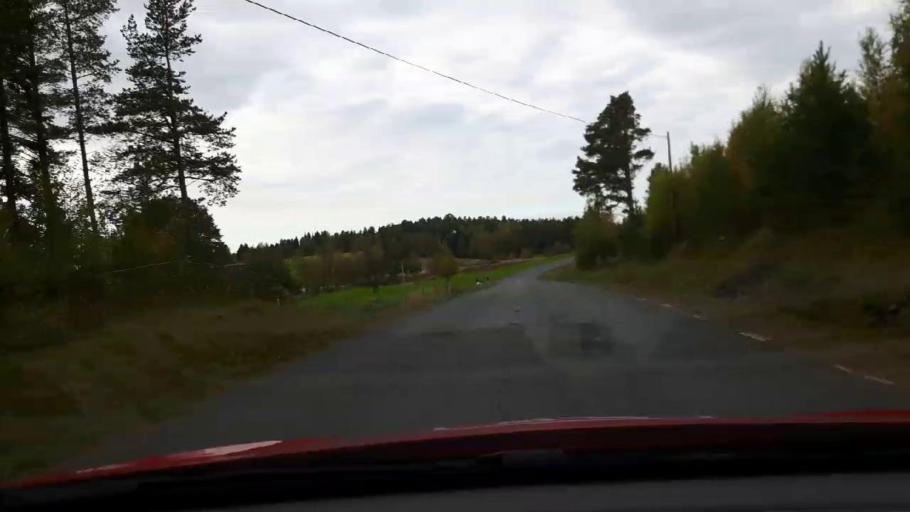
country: SE
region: Jaemtland
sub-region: Krokoms Kommun
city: Krokom
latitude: 63.1994
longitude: 14.1262
